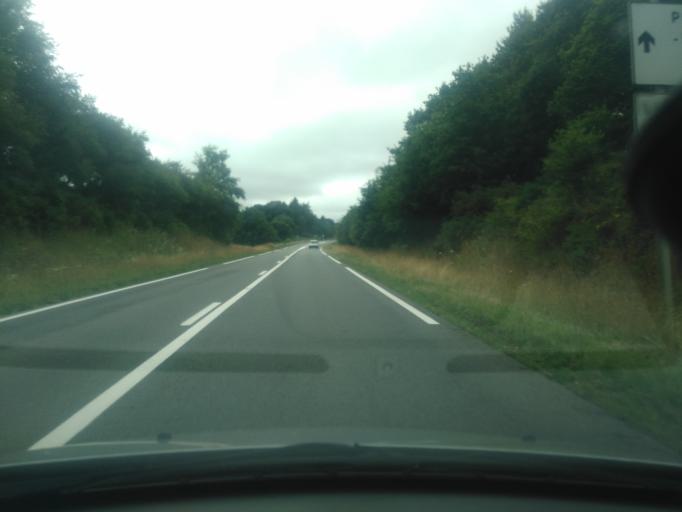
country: FR
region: Brittany
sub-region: Departement des Cotes-d'Armor
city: Saint-Nicolas-du-Pelem
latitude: 48.3030
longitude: -3.1870
